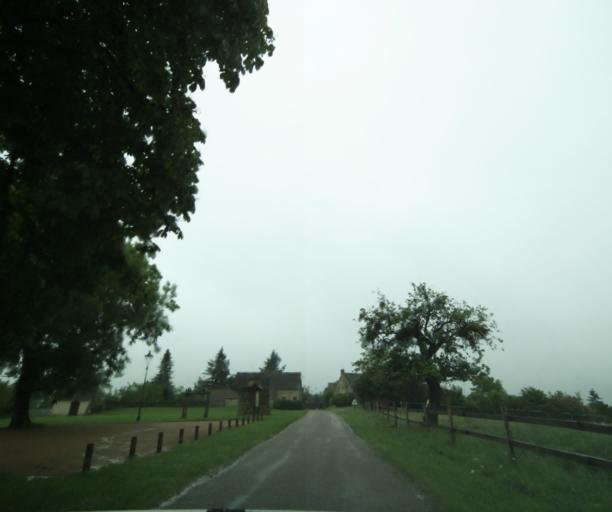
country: FR
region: Bourgogne
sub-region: Departement de Saone-et-Loire
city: Charolles
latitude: 46.3896
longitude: 4.3127
